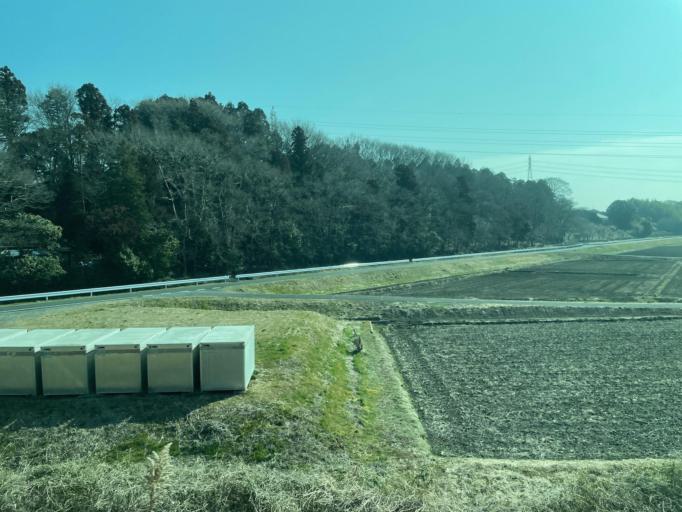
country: JP
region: Ibaraki
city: Hitachi-Naka
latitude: 36.4026
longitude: 140.4831
